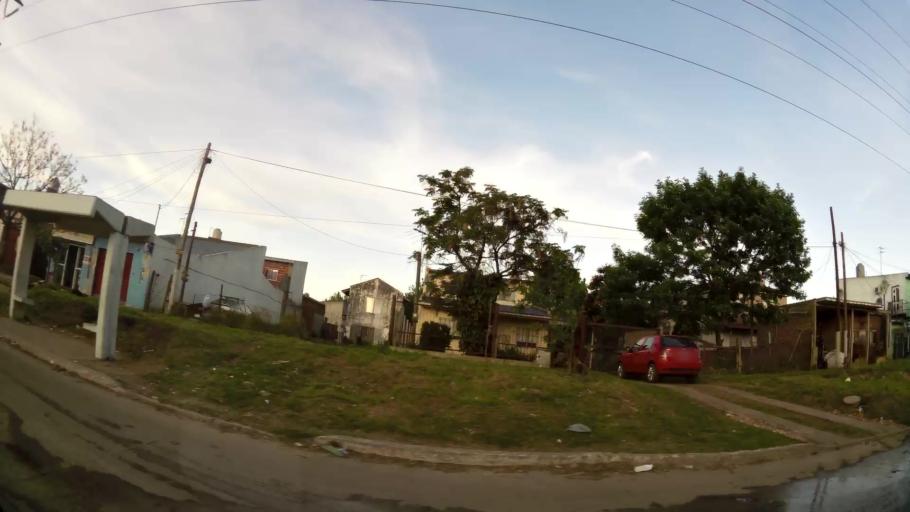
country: AR
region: Buenos Aires
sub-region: Partido de Quilmes
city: Quilmes
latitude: -34.7857
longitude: -58.2209
